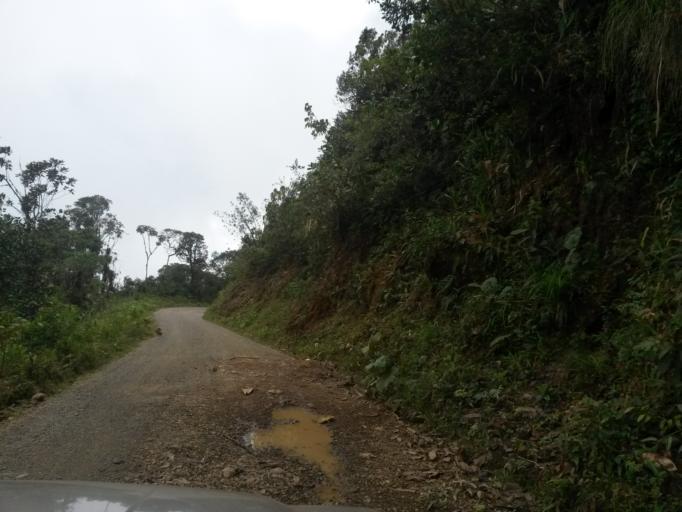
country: CO
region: Cauca
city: Villa Rica
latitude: 2.6674
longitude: -76.9051
